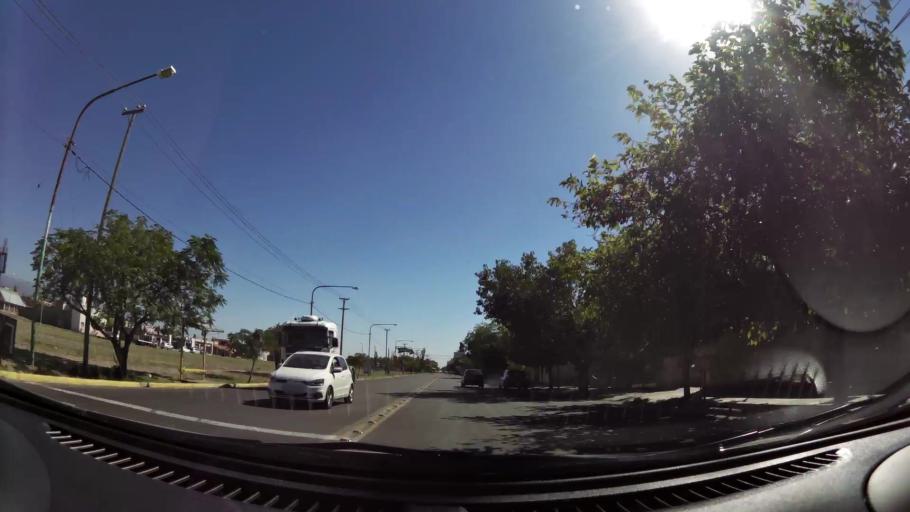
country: AR
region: Mendoza
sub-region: Departamento de Maipu
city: Maipu
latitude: -32.9679
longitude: -68.7921
